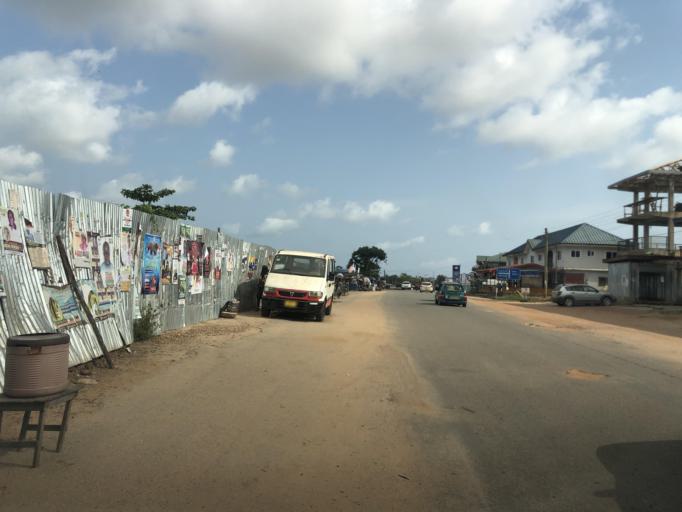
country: GH
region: Central
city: Cape Coast
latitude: 5.1423
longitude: -1.2839
